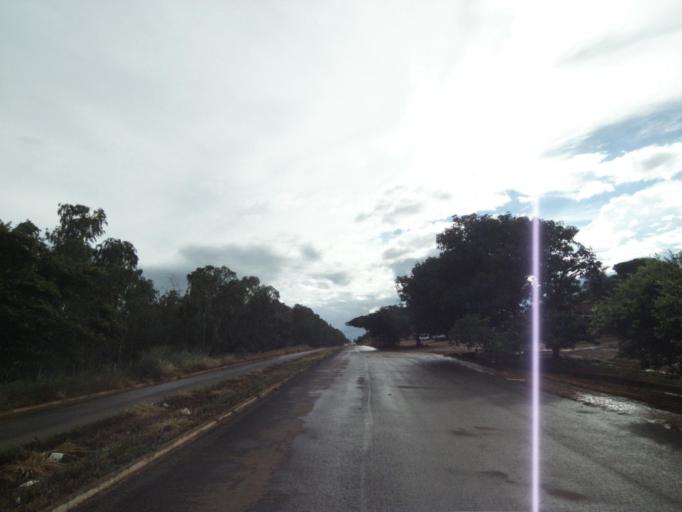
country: BR
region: Goias
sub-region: Itaberai
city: Itaberai
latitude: -15.9213
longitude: -49.6007
